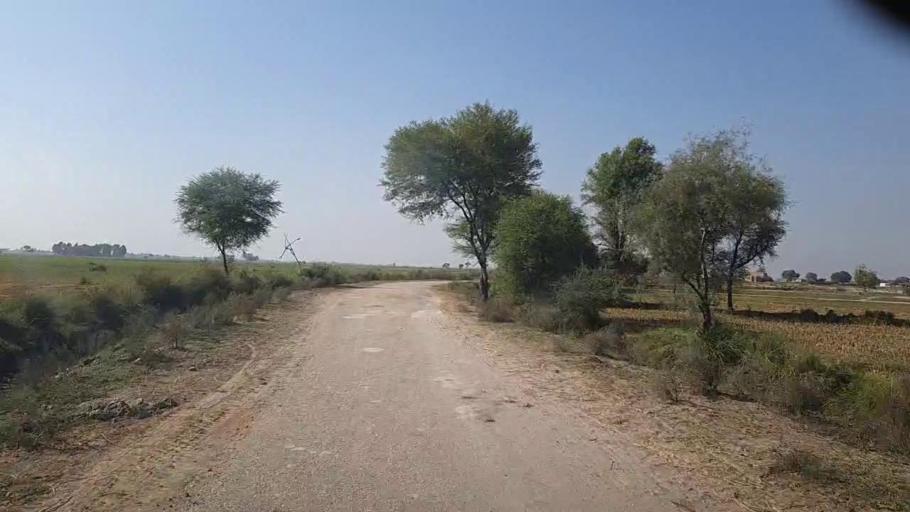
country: PK
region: Sindh
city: Tangwani
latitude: 28.2480
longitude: 68.9449
